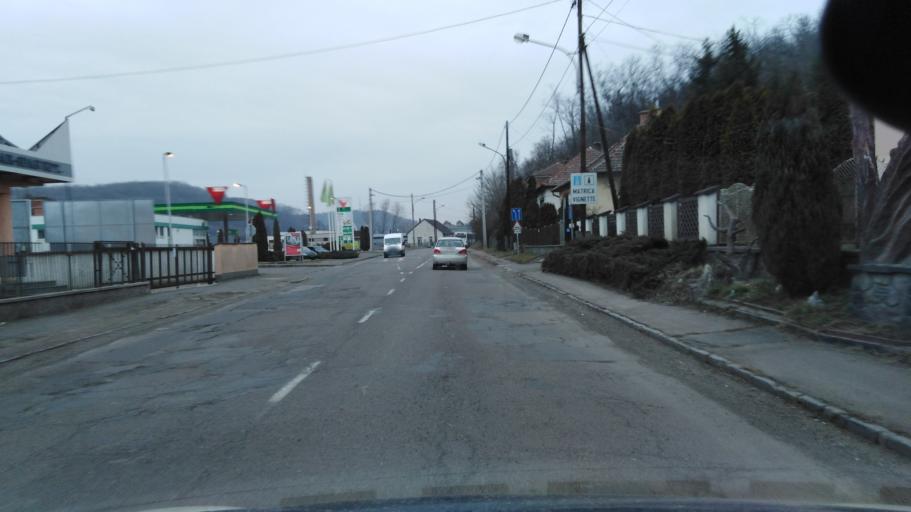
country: HU
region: Nograd
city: Salgotarjan
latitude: 48.0901
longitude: 19.7948
